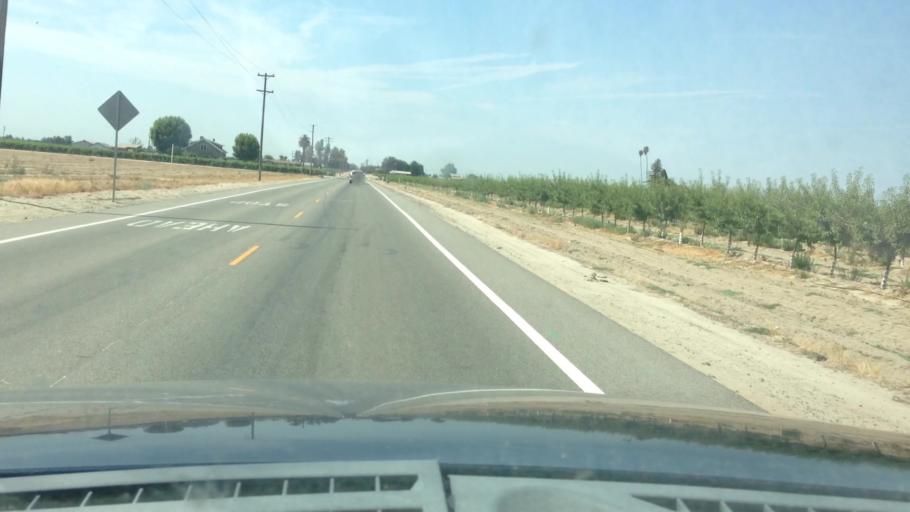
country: US
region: California
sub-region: Fresno County
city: Kingsburg
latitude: 36.5601
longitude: -119.5566
